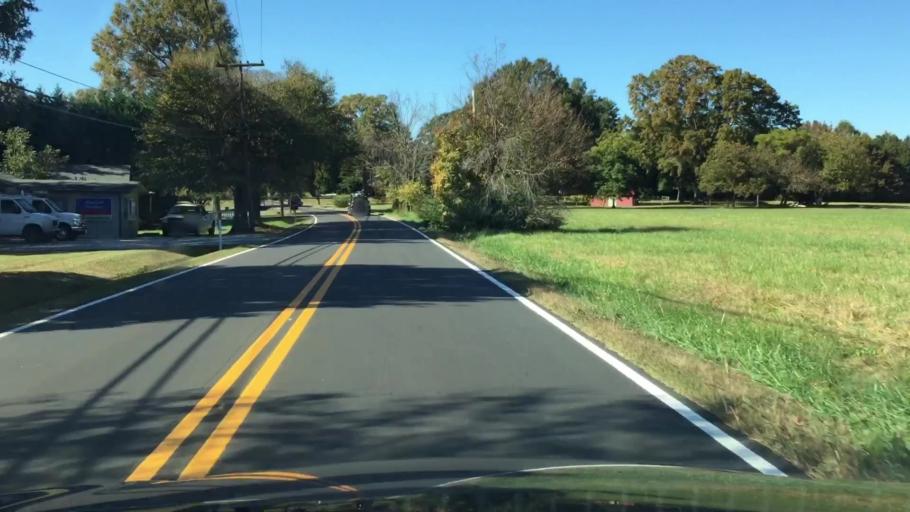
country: US
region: North Carolina
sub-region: Iredell County
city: Mooresville
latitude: 35.5878
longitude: -80.7887
